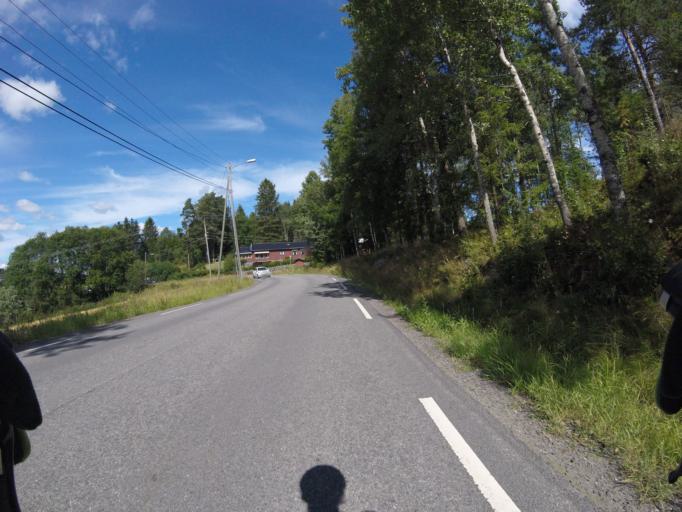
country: NO
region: Akershus
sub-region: Lorenskog
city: Kjenn
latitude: 59.9081
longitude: 10.9588
